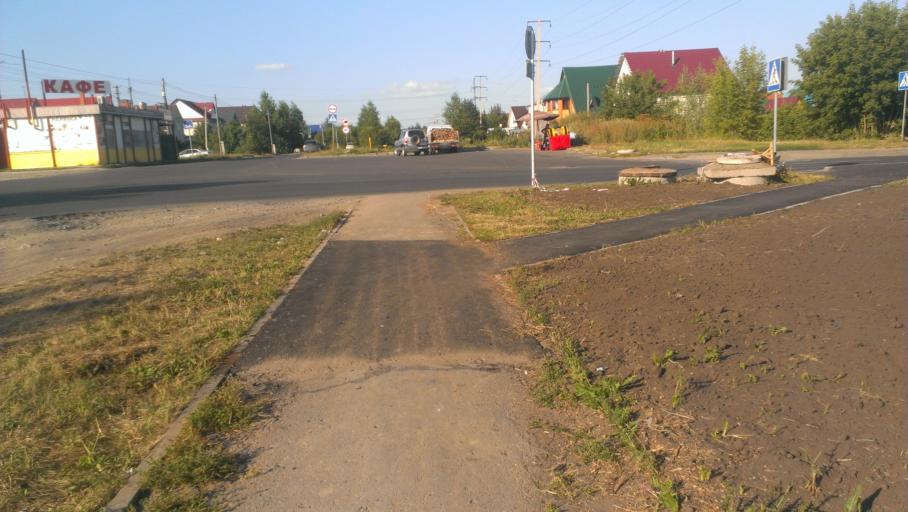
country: RU
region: Altai Krai
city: Novosilikatnyy
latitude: 53.3565
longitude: 83.6369
